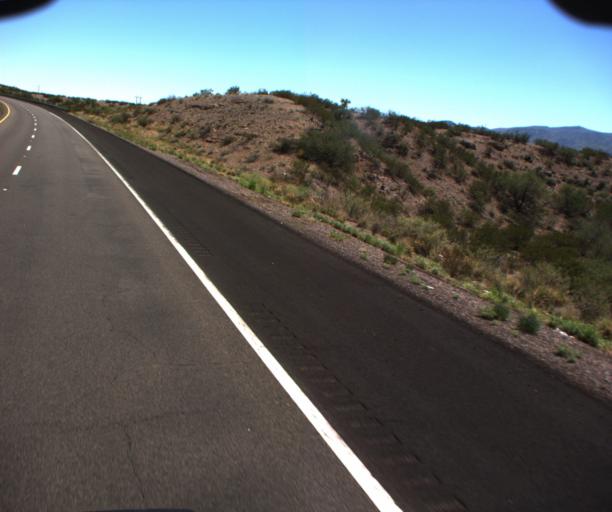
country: US
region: Arizona
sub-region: Greenlee County
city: Clifton
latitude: 32.9956
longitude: -109.2743
